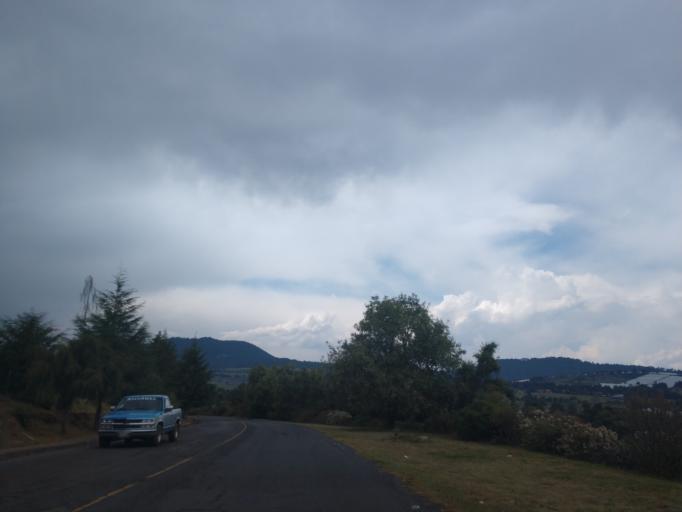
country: MX
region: Jalisco
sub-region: Mazamitla
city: Mazamitla
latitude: 19.9229
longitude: -103.0402
